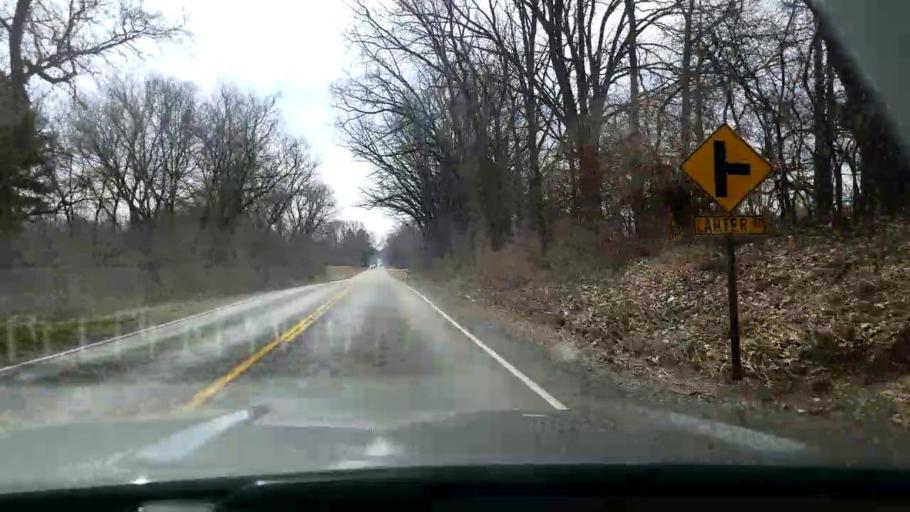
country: US
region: Michigan
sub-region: Jackson County
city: Spring Arbor
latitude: 42.2025
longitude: -84.5210
